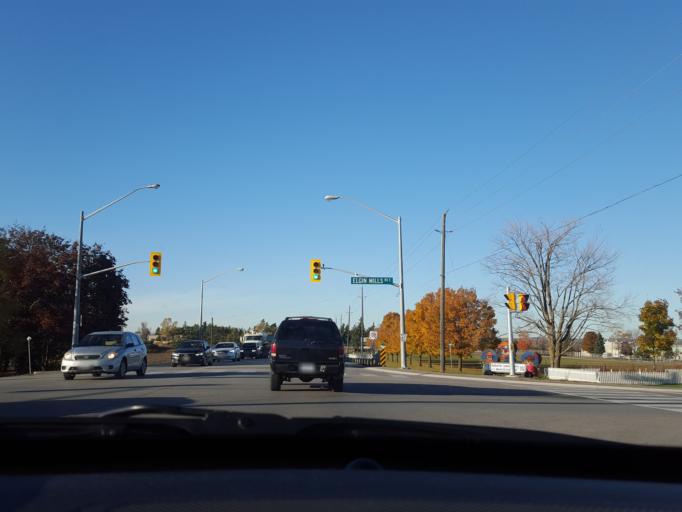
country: CA
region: Ontario
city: Markham
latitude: 43.9215
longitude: -79.2974
